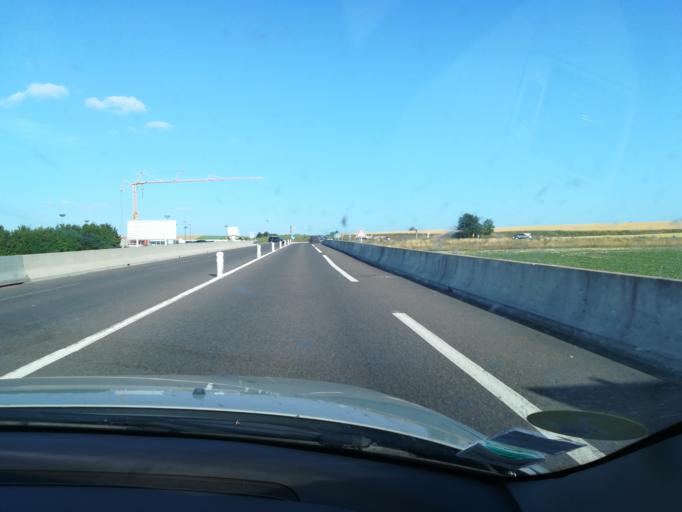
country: FR
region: Champagne-Ardenne
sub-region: Departement de la Marne
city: Bezannes
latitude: 49.2035
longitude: 4.0087
